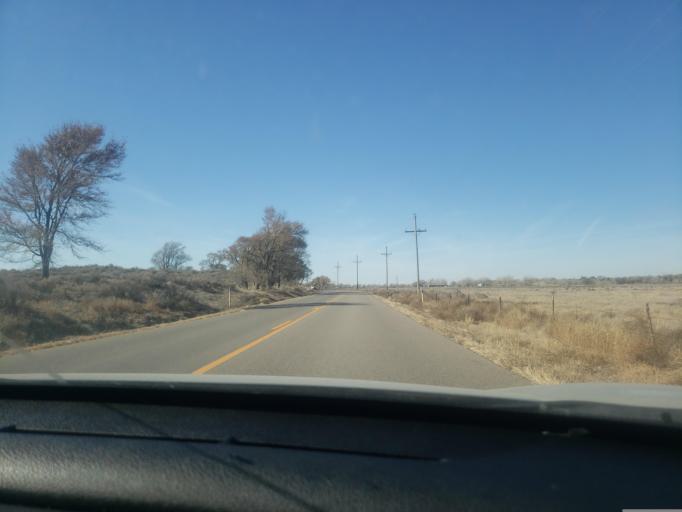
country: US
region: Kansas
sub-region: Finney County
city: Garden City
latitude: 37.9514
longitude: -100.8586
